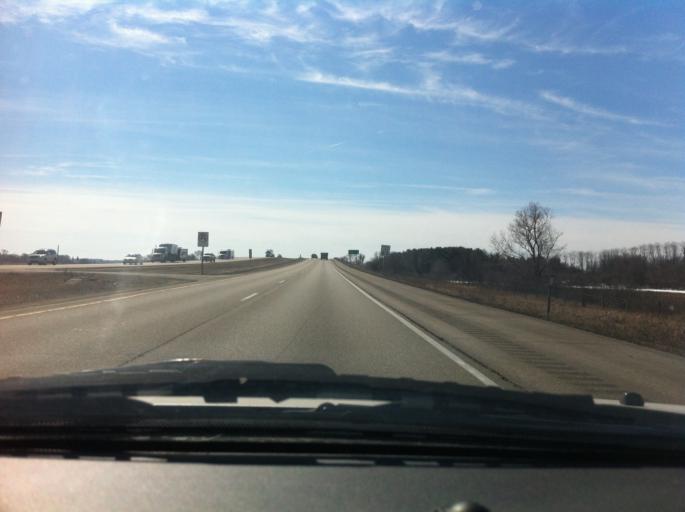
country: US
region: Wisconsin
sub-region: Rock County
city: Janesville
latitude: 42.6772
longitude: -88.9839
